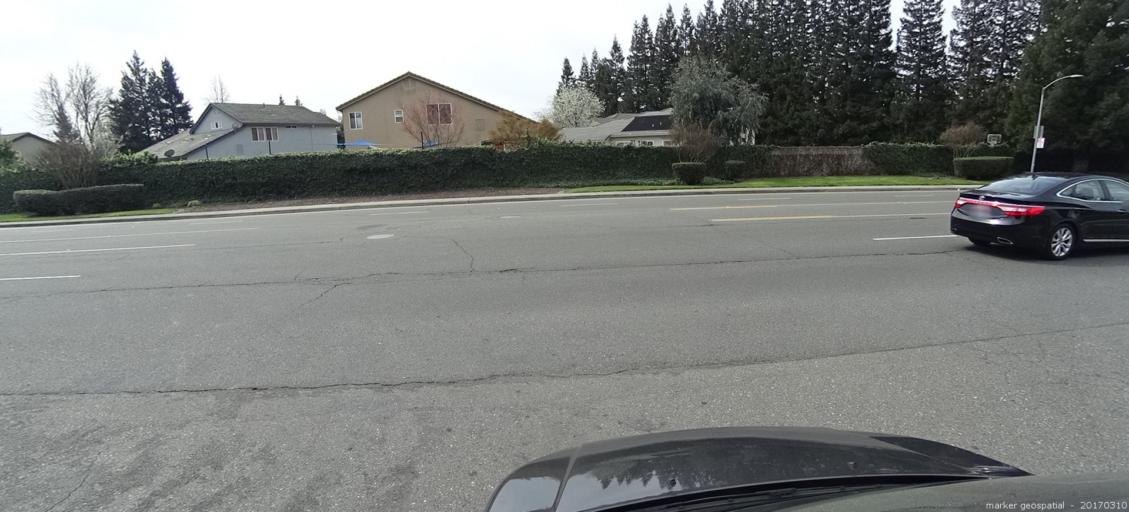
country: US
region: California
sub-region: Sacramento County
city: Parkway
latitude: 38.4912
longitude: -121.5190
